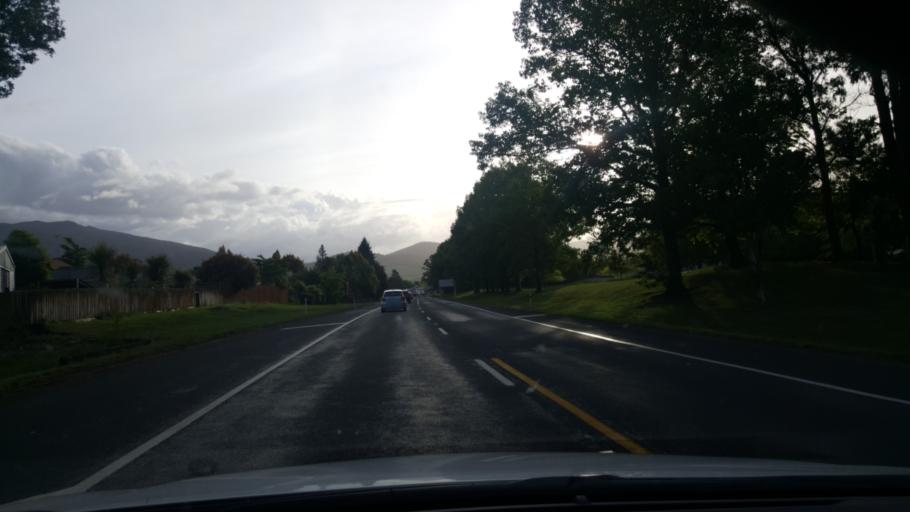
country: NZ
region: Waikato
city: Turangi
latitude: -38.9881
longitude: 175.8165
